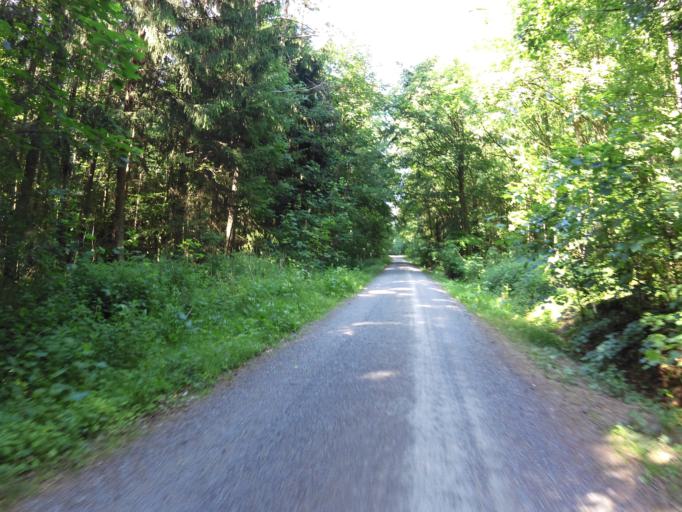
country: DE
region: Bavaria
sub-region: Regierungsbezirk Unterfranken
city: Kleinrinderfeld
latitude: 49.7198
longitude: 9.8642
